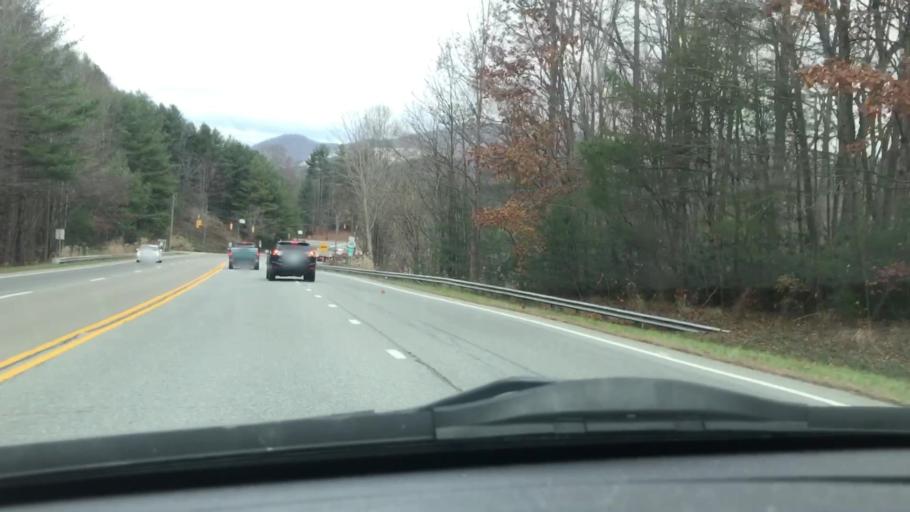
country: US
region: North Carolina
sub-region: Mitchell County
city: Spruce Pine
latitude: 35.9082
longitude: -82.0741
